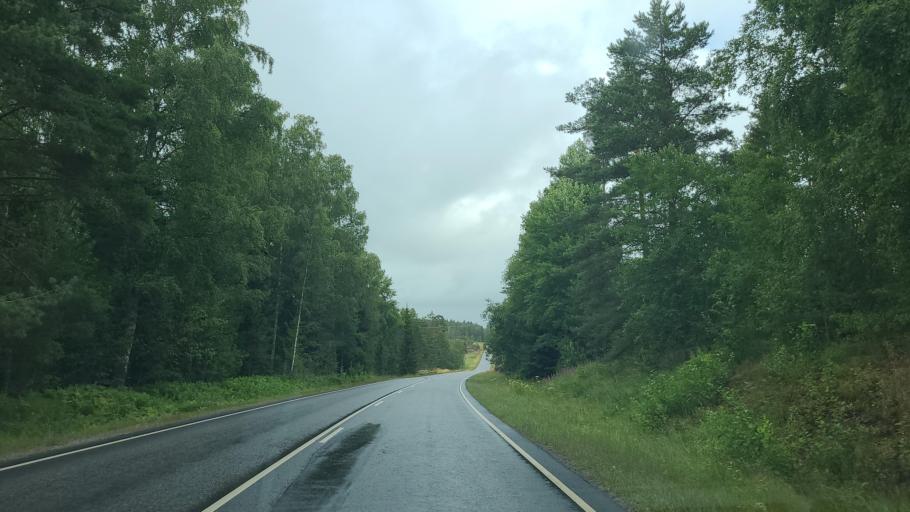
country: FI
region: Varsinais-Suomi
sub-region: Turku
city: Sauvo
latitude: 60.2367
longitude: 22.6057
